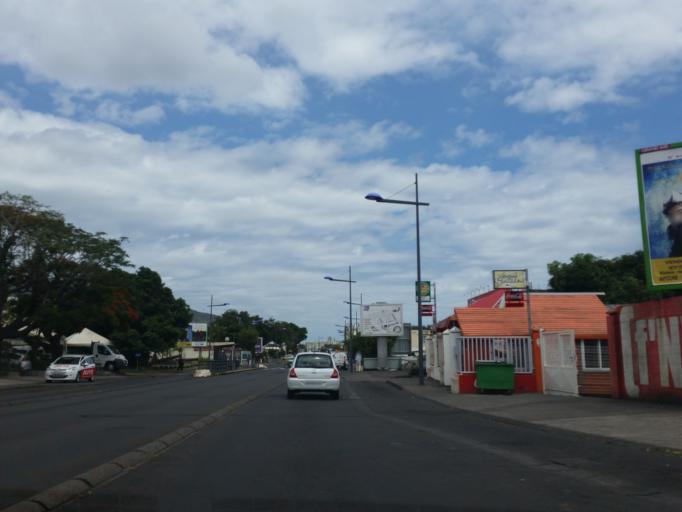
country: RE
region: Reunion
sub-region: Reunion
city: Saint-Denis
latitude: -20.8889
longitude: 55.4756
